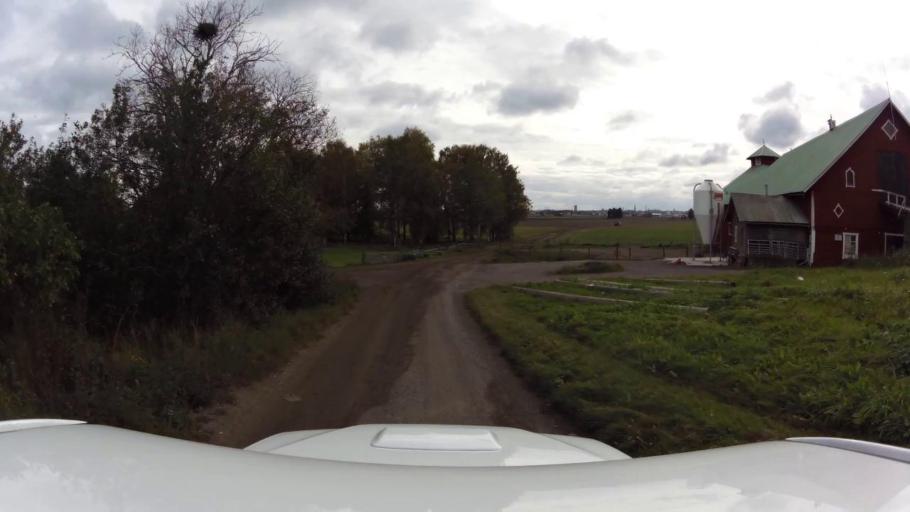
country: SE
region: OEstergoetland
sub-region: Linkopings Kommun
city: Ekangen
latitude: 58.4482
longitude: 15.5858
